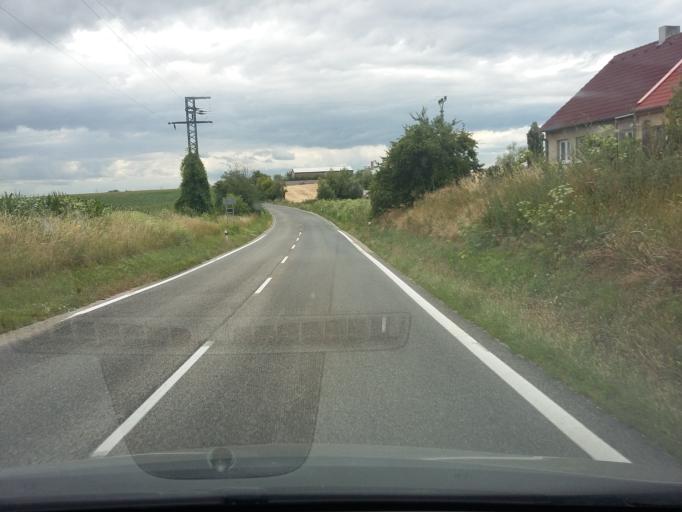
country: SK
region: Trnavsky
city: Vrbove
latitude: 48.6101
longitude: 17.7146
